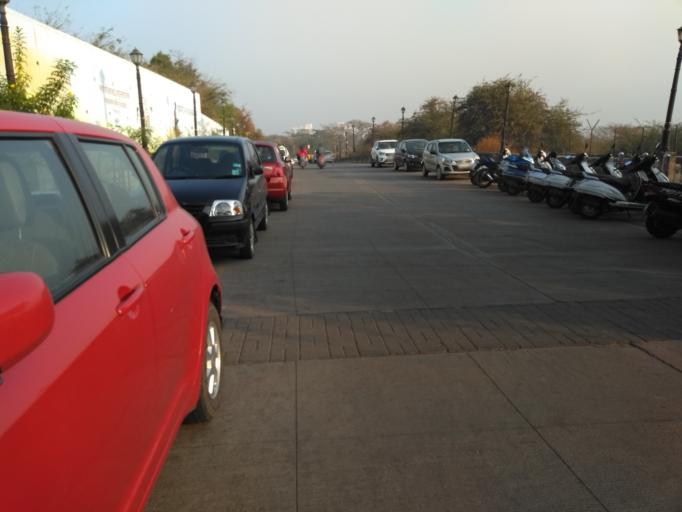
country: IN
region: Maharashtra
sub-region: Pune Division
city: Pune
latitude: 18.4765
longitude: 73.8447
